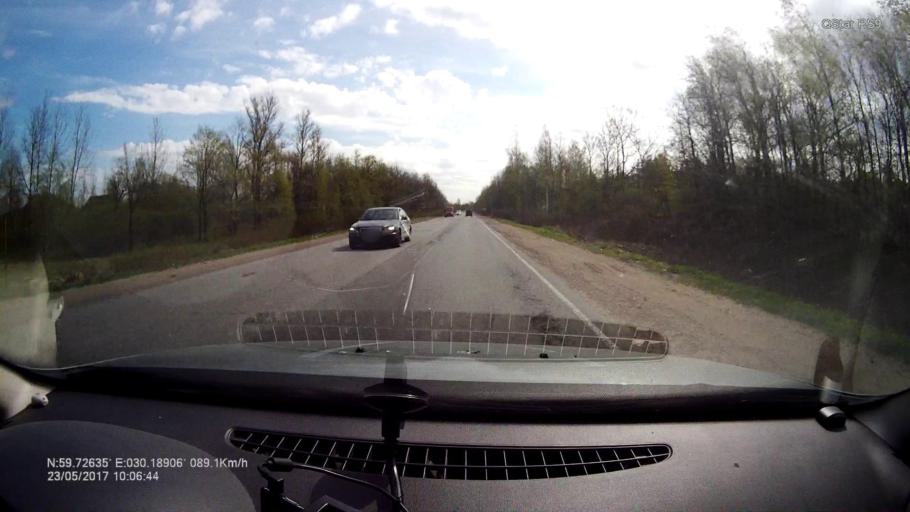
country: RU
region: St.-Petersburg
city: Gorelovo
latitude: 59.7264
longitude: 30.1899
